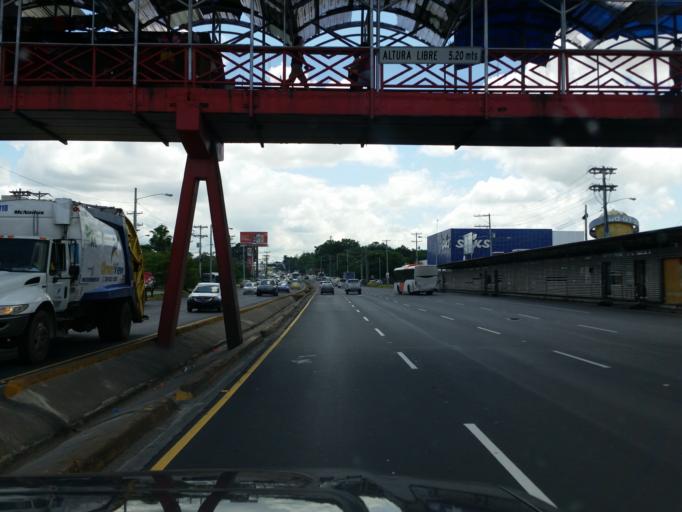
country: PA
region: Panama
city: San Miguelito
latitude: 9.0506
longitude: -79.4507
